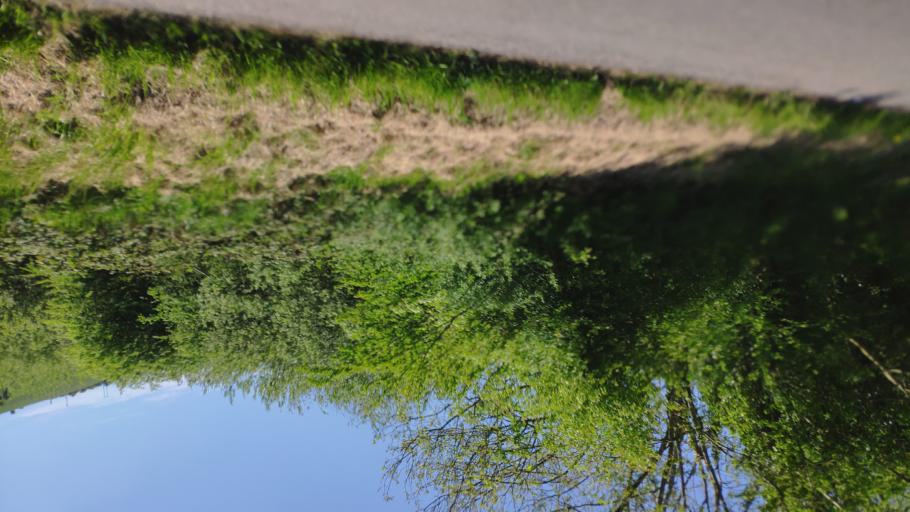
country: IE
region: Munster
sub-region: County Cork
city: Blarney
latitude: 51.9147
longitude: -8.5196
